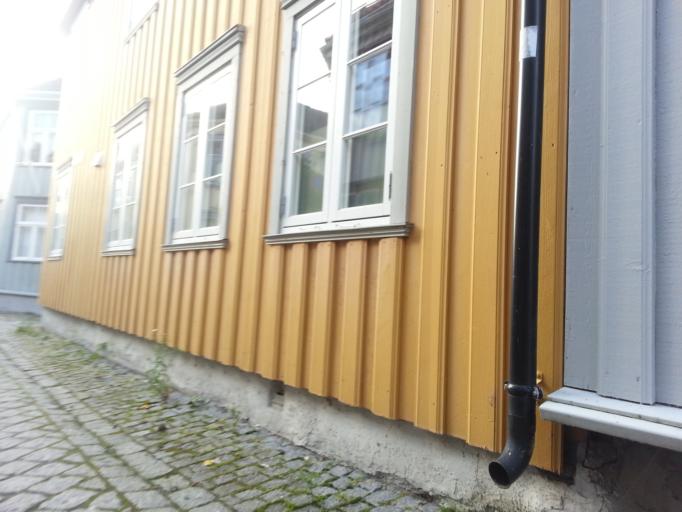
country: NO
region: Sor-Trondelag
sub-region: Trondheim
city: Trondheim
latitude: 63.4313
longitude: 10.3889
